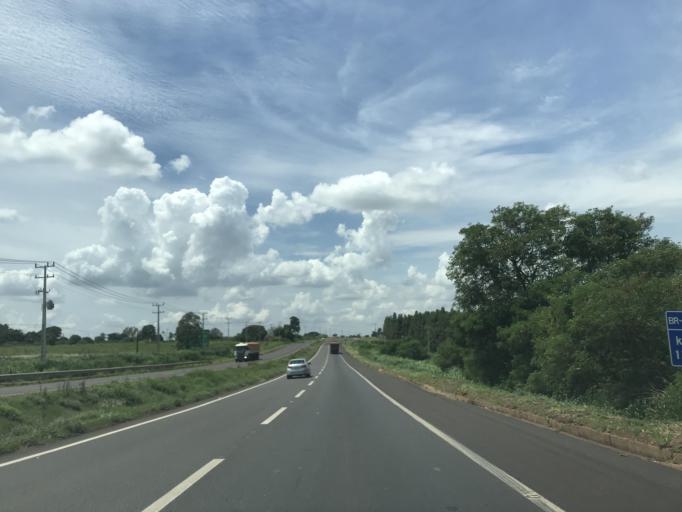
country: BR
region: Parana
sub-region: Alto Parana
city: Alto Parana
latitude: -23.2154
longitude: -52.1867
